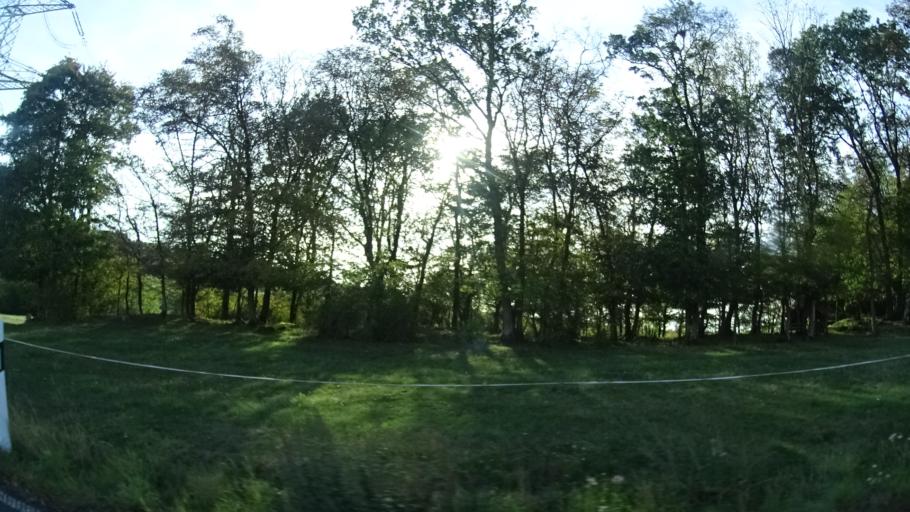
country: DE
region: Hesse
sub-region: Regierungsbezirk Giessen
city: Freiensteinau
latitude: 50.3913
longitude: 9.4428
